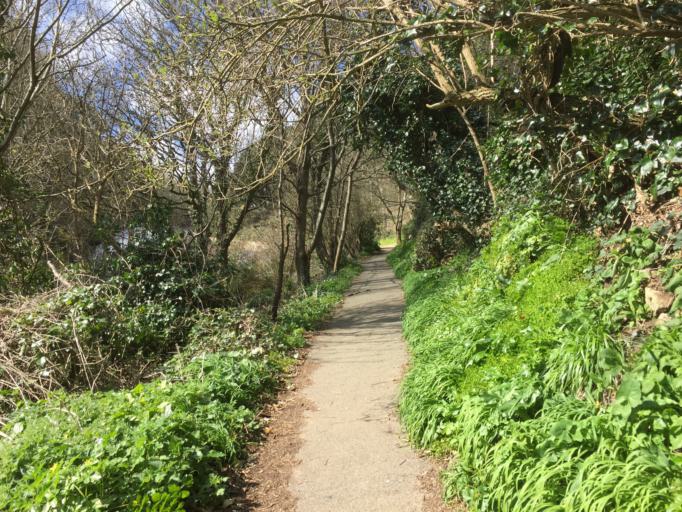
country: GG
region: St Peter Port
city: Saint Peter Port
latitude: 49.4272
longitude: -2.5492
